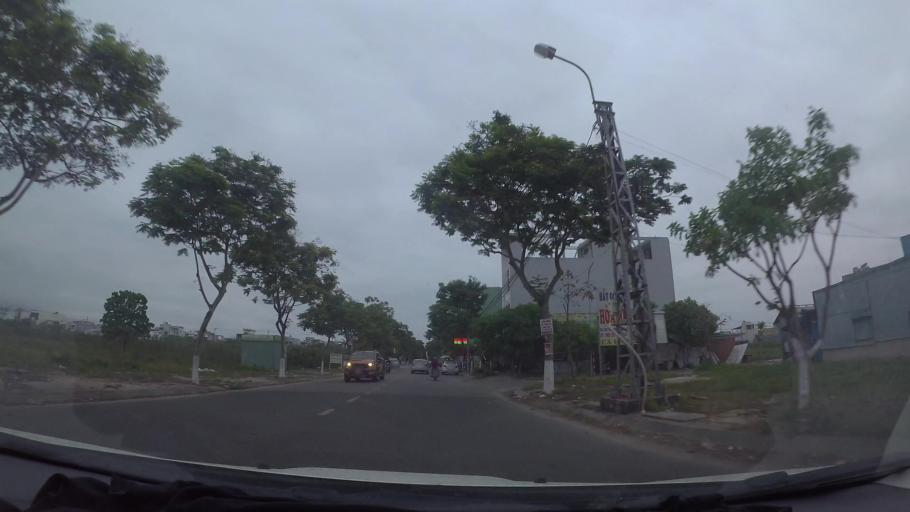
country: VN
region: Da Nang
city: Lien Chieu
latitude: 16.0754
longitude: 108.1588
